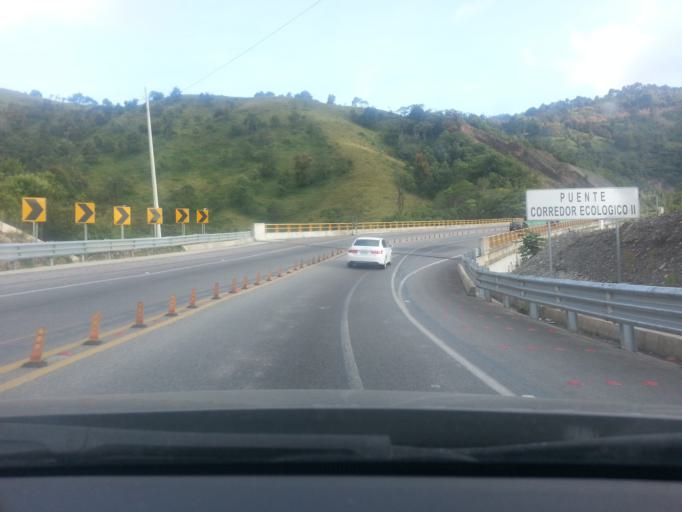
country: MX
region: Puebla
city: Necaxa
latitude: 20.2310
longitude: -98.0281
